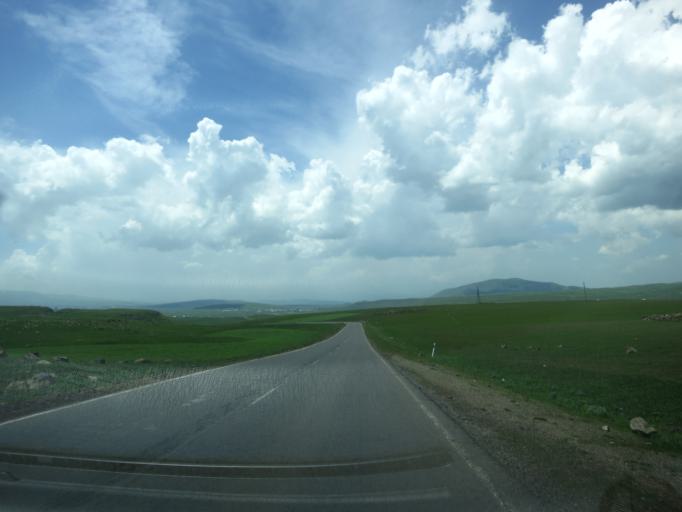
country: GE
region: Samtskhe-Javakheti
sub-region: Ninotsminda
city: Ninotsminda
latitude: 41.2949
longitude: 43.6840
